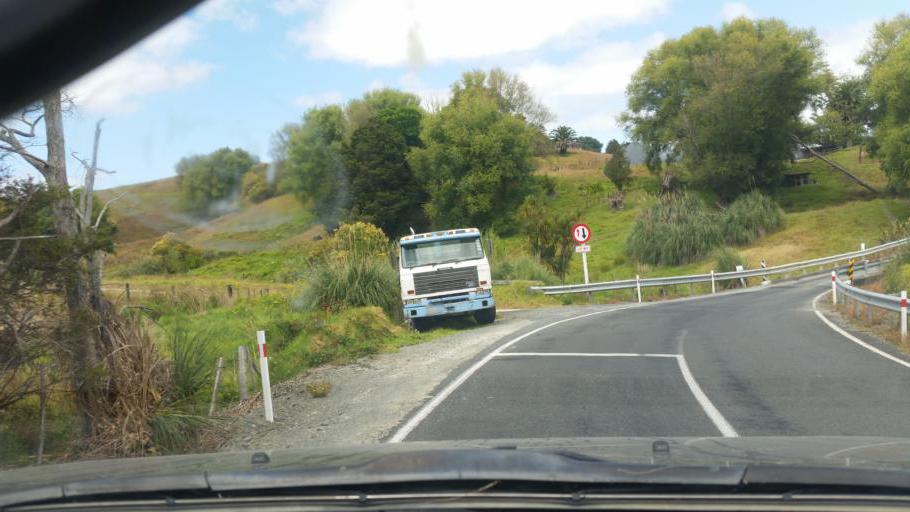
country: NZ
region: Auckland
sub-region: Auckland
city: Wellsford
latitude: -36.1293
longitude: 174.3274
